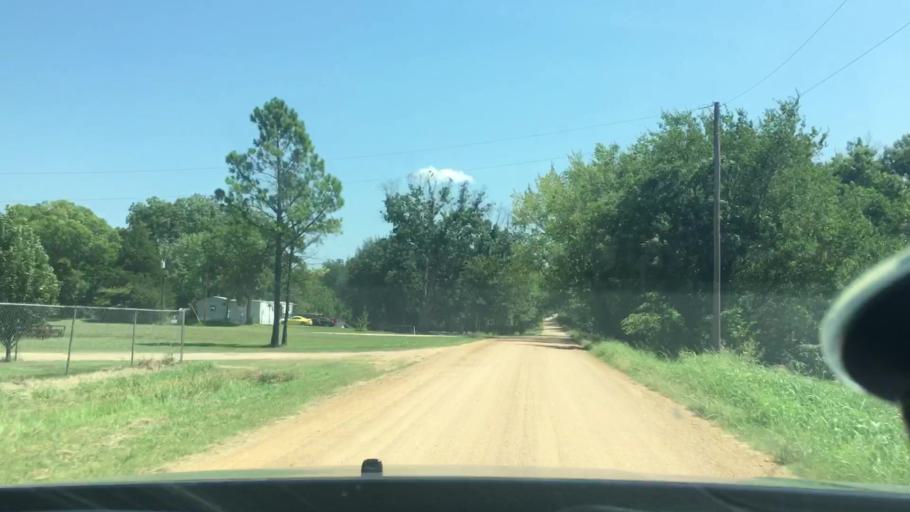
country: US
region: Oklahoma
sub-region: Coal County
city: Coalgate
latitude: 34.3681
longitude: -96.4289
